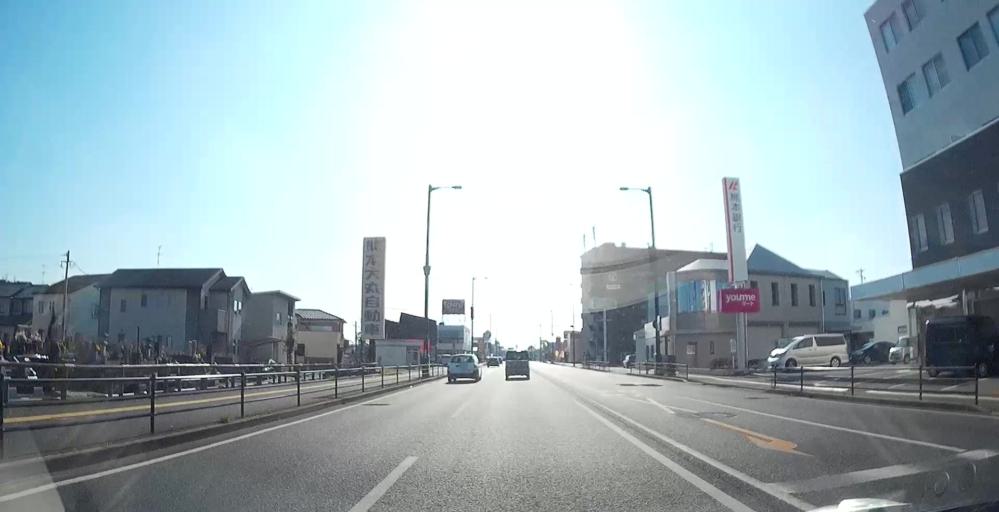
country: JP
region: Kumamoto
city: Kumamoto
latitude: 32.7689
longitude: 130.6927
